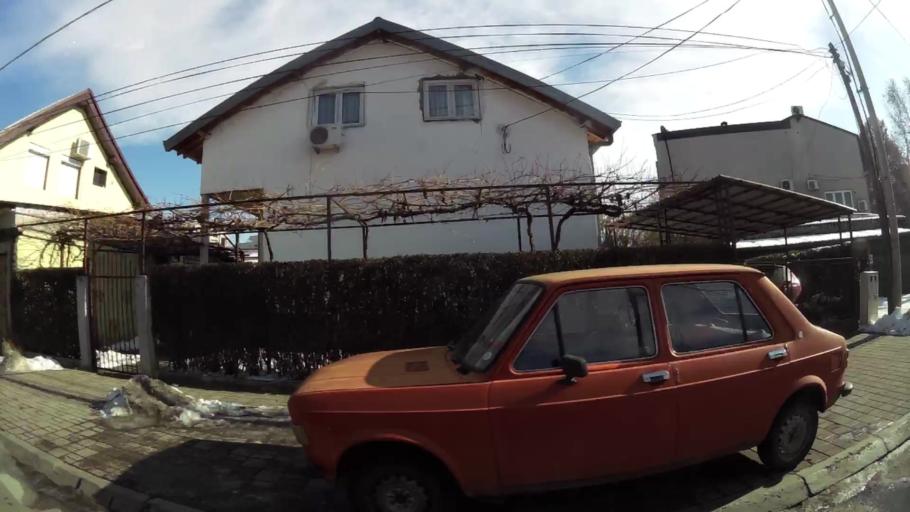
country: MK
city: Krushopek
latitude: 42.0065
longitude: 21.3653
